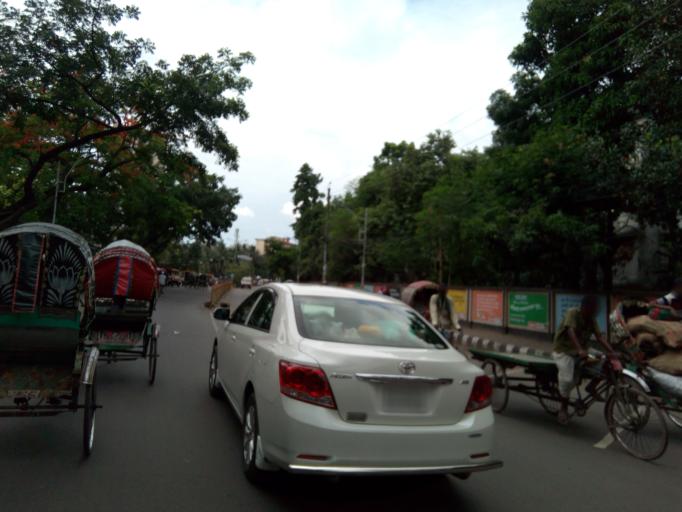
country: BD
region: Dhaka
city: Azimpur
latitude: 23.7312
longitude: 90.3870
